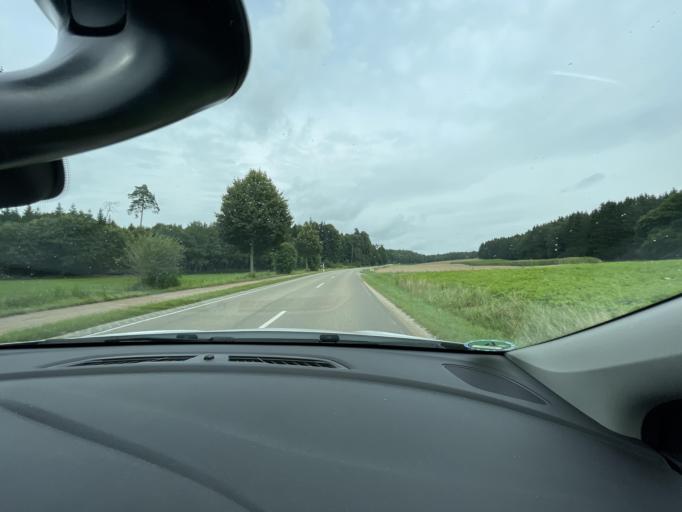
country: DE
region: Bavaria
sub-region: Swabia
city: Thierhaupten
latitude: 48.5637
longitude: 10.9379
